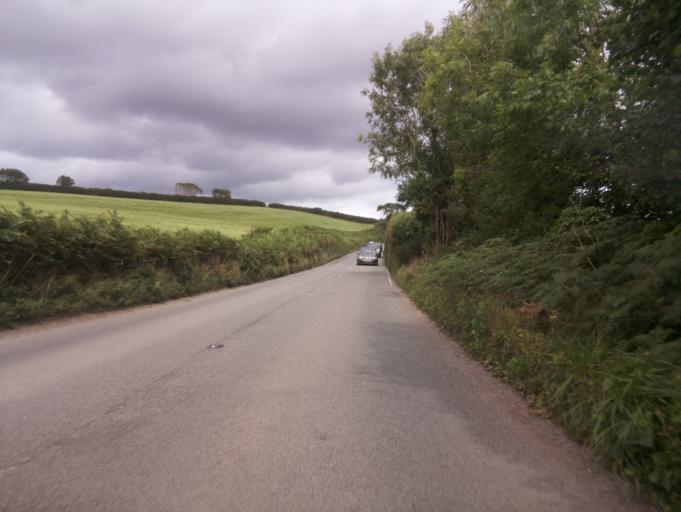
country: GB
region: England
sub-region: Devon
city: Totnes
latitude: 50.3793
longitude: -3.7111
